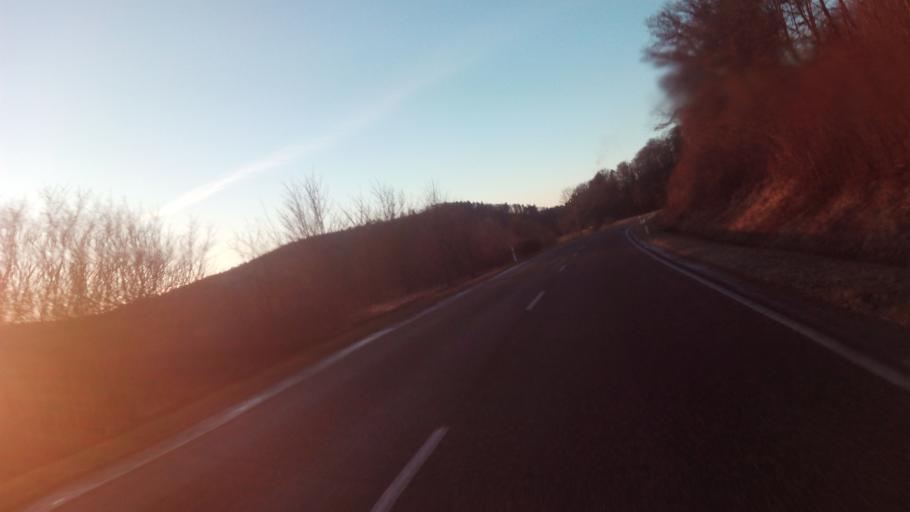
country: DE
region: Baden-Wuerttemberg
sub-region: Tuebingen Region
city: Schelklingen
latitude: 48.3523
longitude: 9.7519
